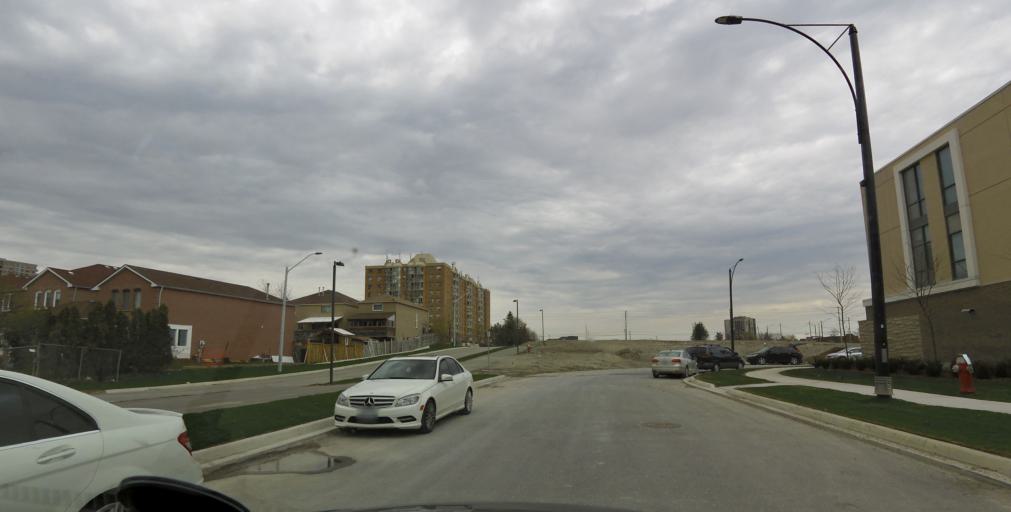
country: CA
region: Ontario
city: Mississauga
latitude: 43.6067
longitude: -79.6576
